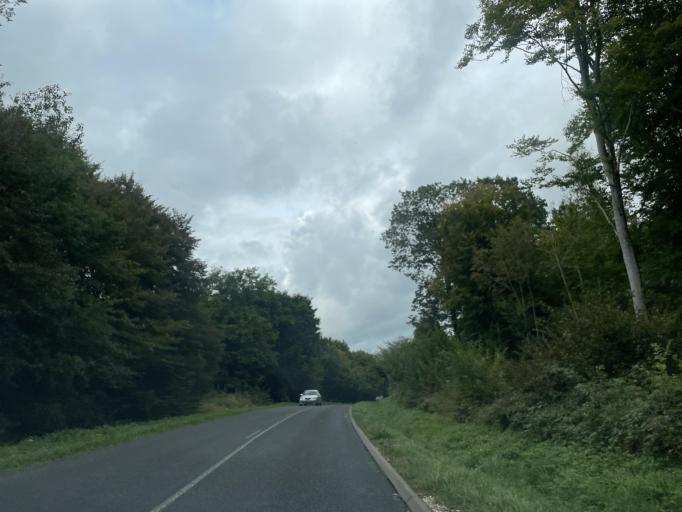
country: FR
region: Ile-de-France
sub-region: Departement de Seine-et-Marne
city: Saint-Jean-les-Deux-Jumeaux
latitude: 48.9152
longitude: 3.0135
